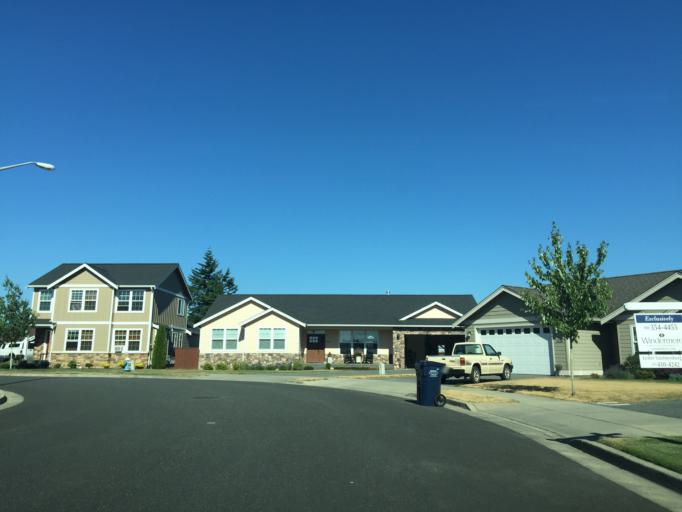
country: US
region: Washington
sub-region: Whatcom County
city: Lynden
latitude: 48.9607
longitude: -122.4198
